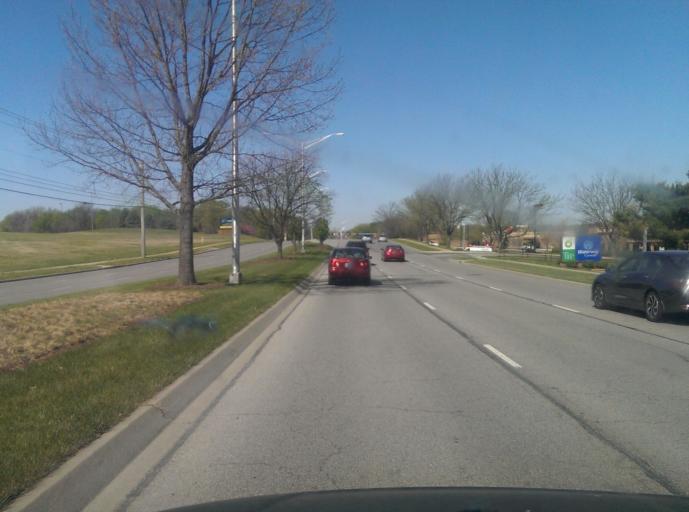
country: US
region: Kansas
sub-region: Johnson County
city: Lenexa
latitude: 38.9275
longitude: -94.7261
